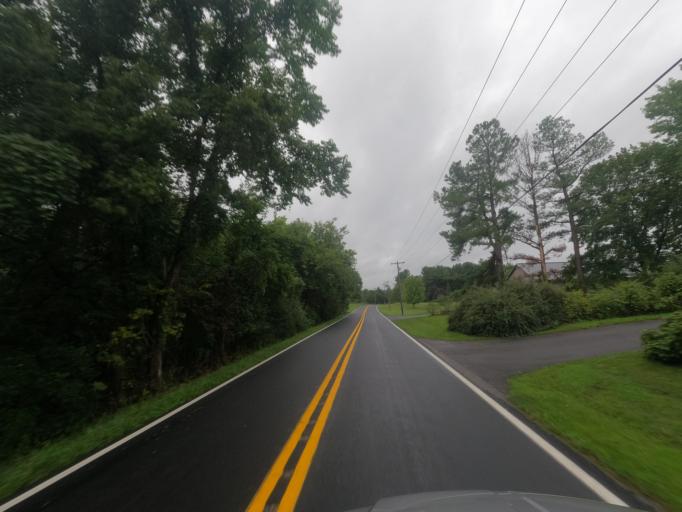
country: US
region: Maryland
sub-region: Washington County
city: Wilson-Conococheague
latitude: 39.6203
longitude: -77.9903
